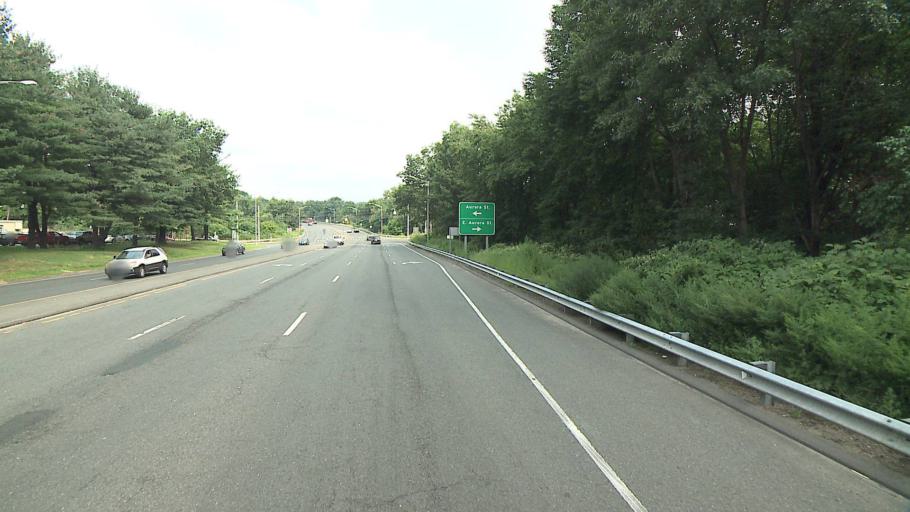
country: US
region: Connecticut
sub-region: New Haven County
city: Waterbury
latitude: 41.5702
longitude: -73.0594
